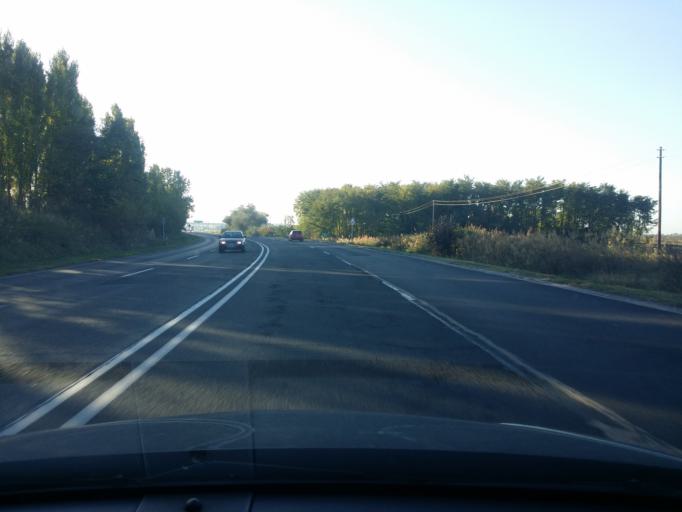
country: HU
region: Bacs-Kiskun
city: Kecskemet
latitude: 46.9476
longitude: 19.6518
